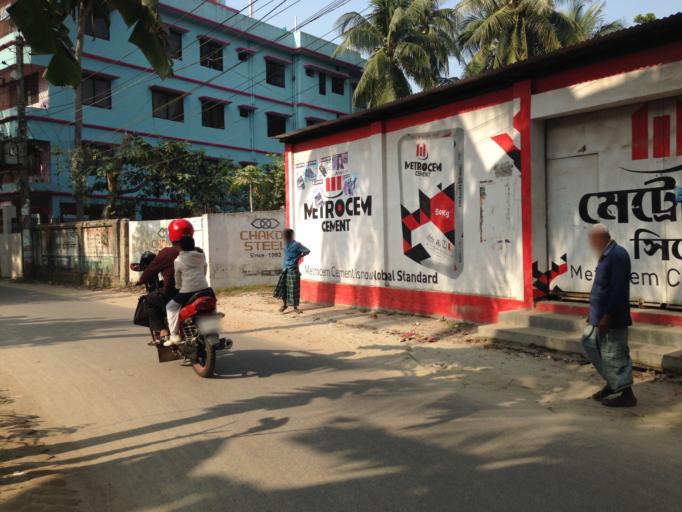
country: BD
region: Chittagong
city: Lakshmipur
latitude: 22.9368
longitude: 90.8320
